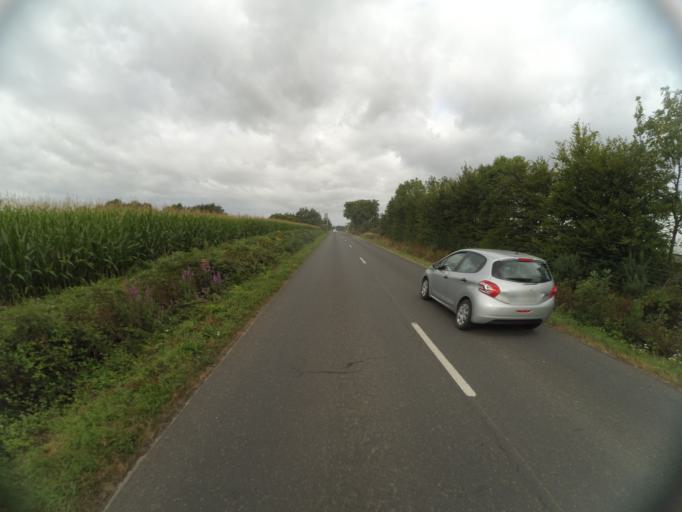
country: FR
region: Pays de la Loire
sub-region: Departement de Maine-et-Loire
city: Saint-Crespin-sur-Moine
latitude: 47.0791
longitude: -1.2117
